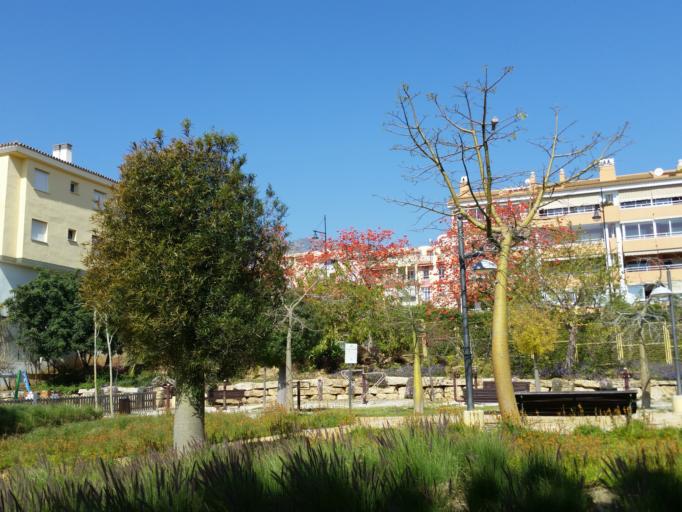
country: ES
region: Andalusia
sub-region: Provincia de Malaga
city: Torremolinos
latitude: 36.6030
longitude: -4.5291
